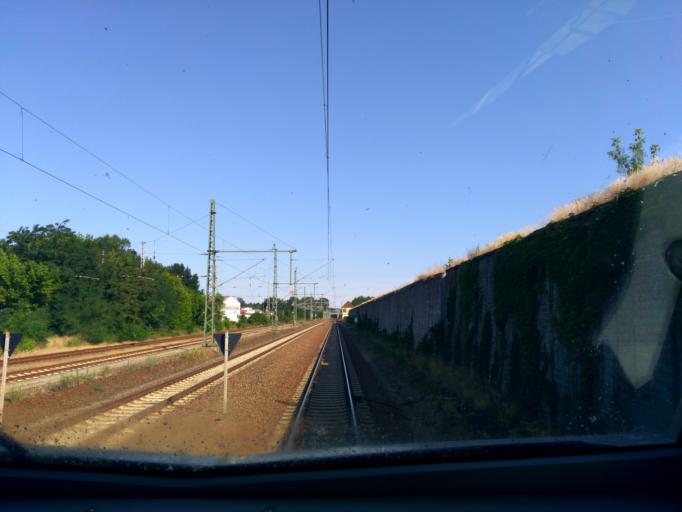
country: DE
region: Brandenburg
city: Luebben
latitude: 51.9420
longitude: 13.8736
